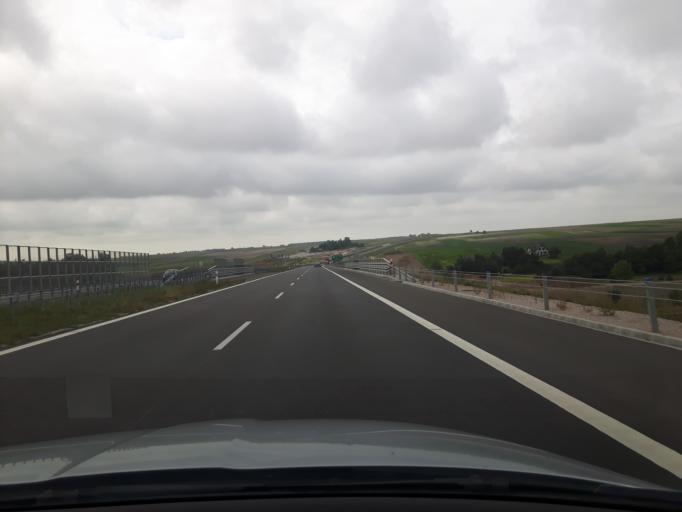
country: PL
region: Swietokrzyskie
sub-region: Powiat jedrzejowski
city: Sobkow
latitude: 50.7116
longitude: 20.4062
